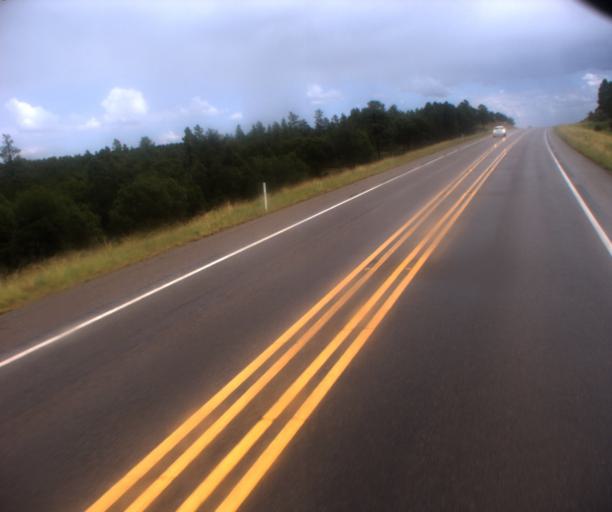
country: US
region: Arizona
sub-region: Navajo County
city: Heber-Overgaard
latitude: 34.3672
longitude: -110.3689
